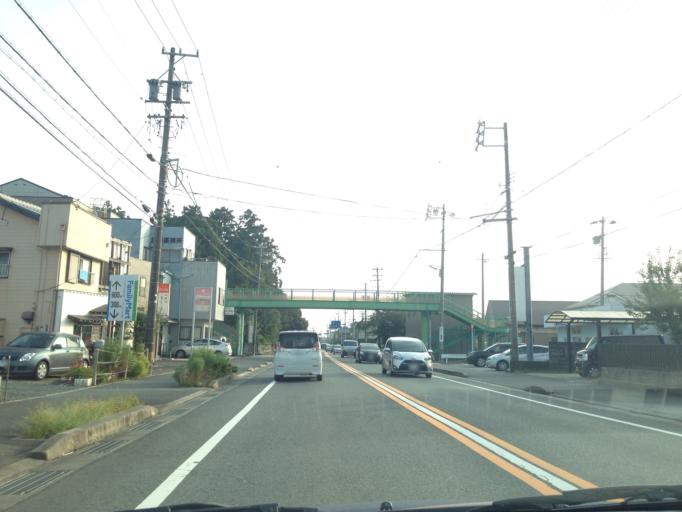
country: JP
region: Aichi
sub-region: Tokai-shi
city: Toyokawa
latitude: 34.8501
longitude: 137.4193
